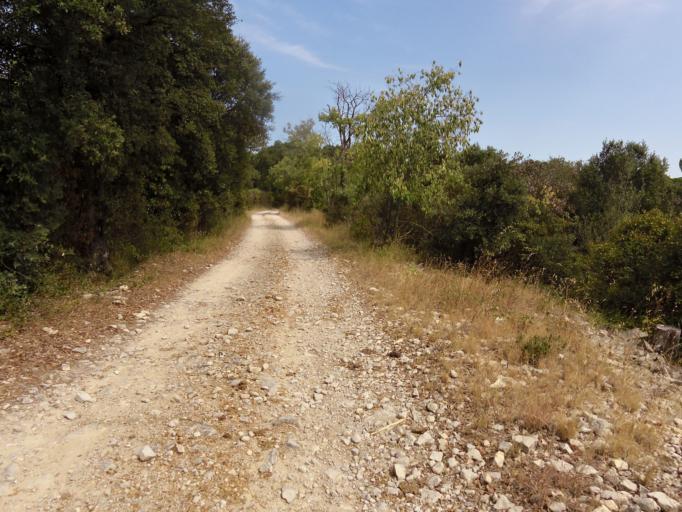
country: FR
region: Languedoc-Roussillon
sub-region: Departement du Gard
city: Congenies
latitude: 43.7561
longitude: 4.1605
